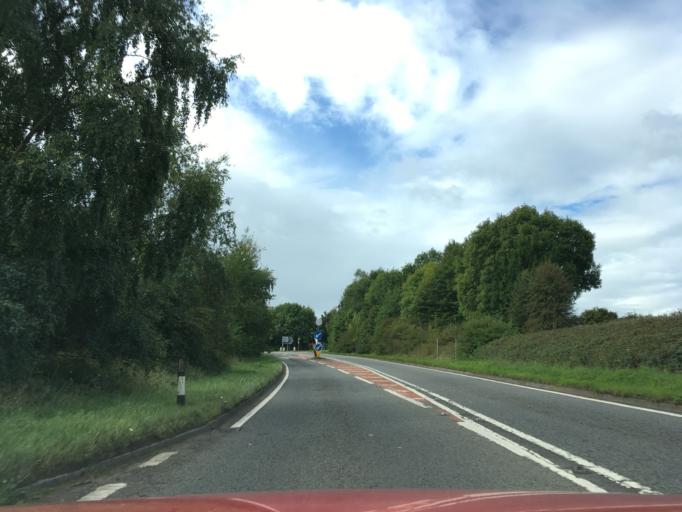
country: GB
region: Wales
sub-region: Monmouthshire
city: Chepstow
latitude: 51.6512
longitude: -2.6562
